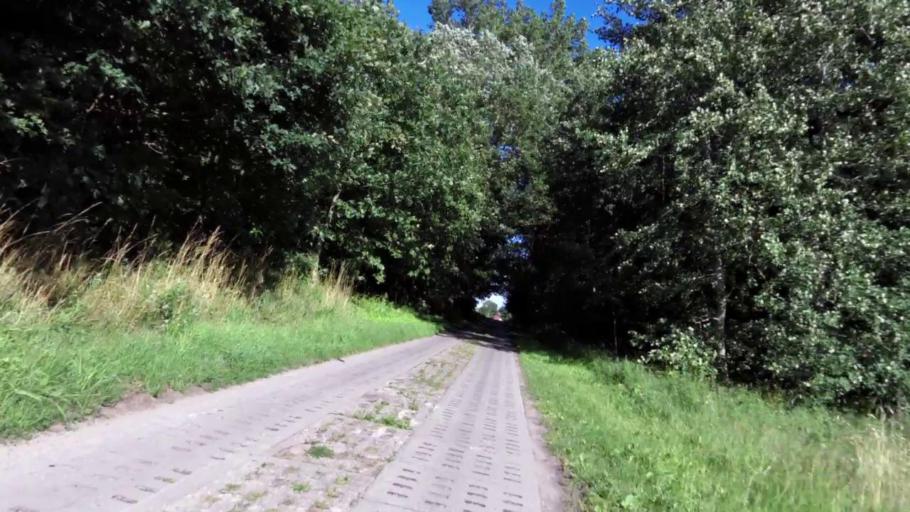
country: PL
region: West Pomeranian Voivodeship
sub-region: Powiat slawienski
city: Slawno
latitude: 54.4614
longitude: 16.7295
